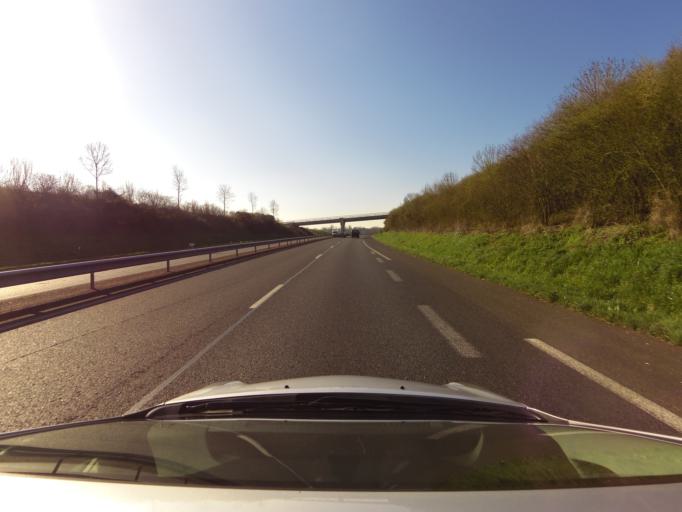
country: FR
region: Lower Normandy
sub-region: Departement de la Manche
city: Saint-Quentin-sur-le-Homme
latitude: 48.6196
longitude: -1.3352
